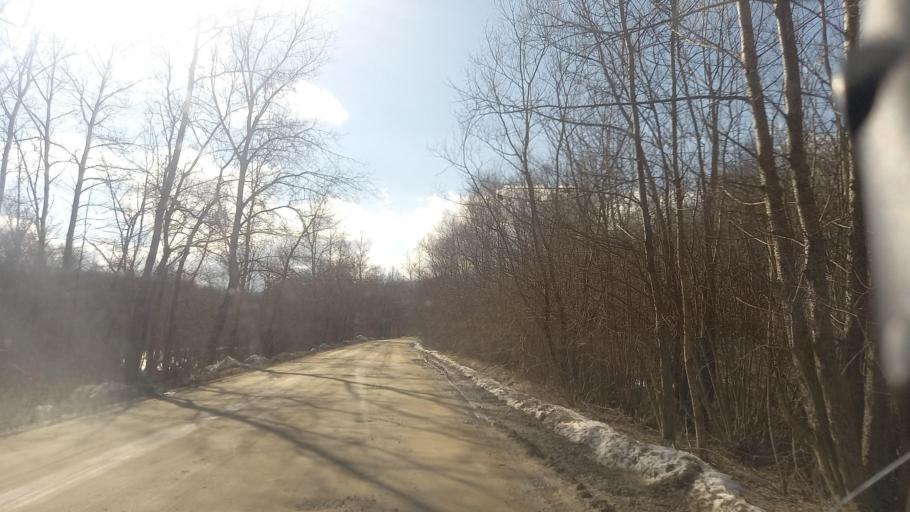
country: RU
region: Krasnodarskiy
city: Smolenskaya
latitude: 44.6649
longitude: 38.7383
